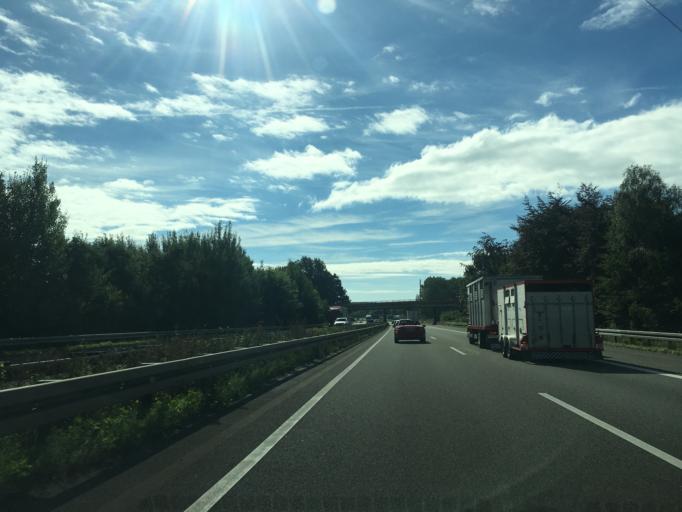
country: DE
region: Lower Saxony
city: Melle
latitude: 52.2007
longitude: 8.3094
